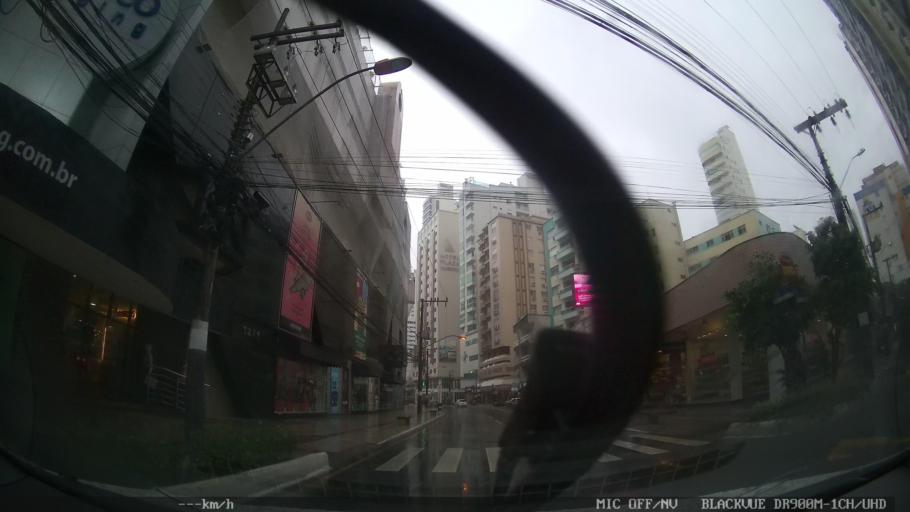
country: BR
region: Santa Catarina
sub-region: Balneario Camboriu
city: Balneario Camboriu
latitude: -26.9845
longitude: -48.6354
